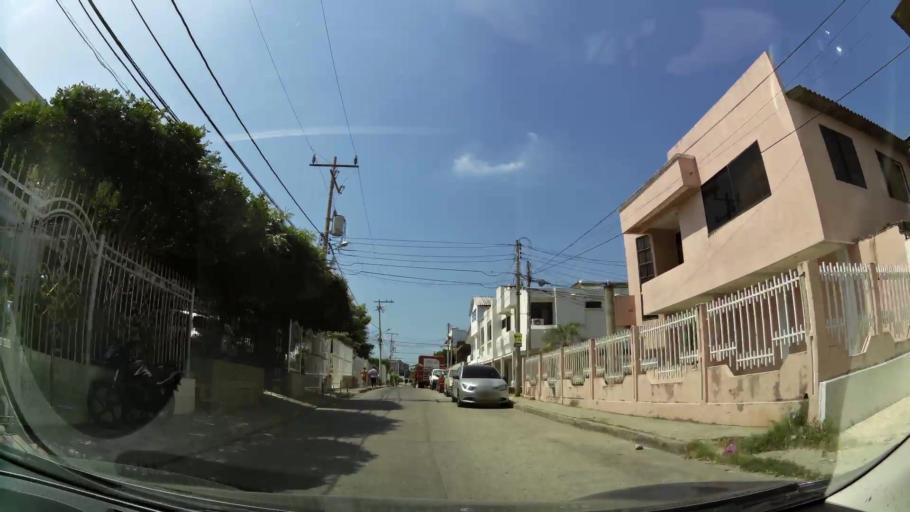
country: CO
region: Bolivar
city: Cartagena
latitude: 10.4007
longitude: -75.4905
